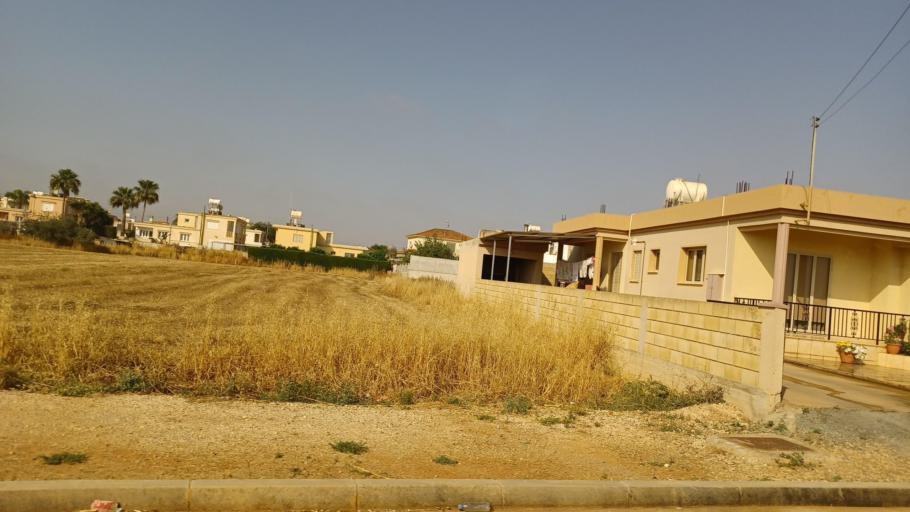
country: CY
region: Ammochostos
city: Avgorou
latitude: 35.0460
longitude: 33.8288
